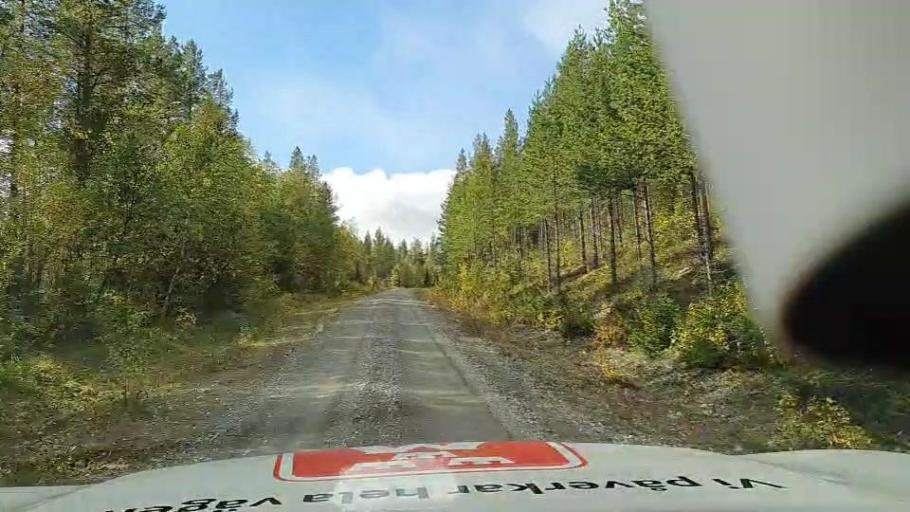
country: SE
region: Jaemtland
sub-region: Are Kommun
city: Jarpen
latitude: 63.1687
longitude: 13.5068
